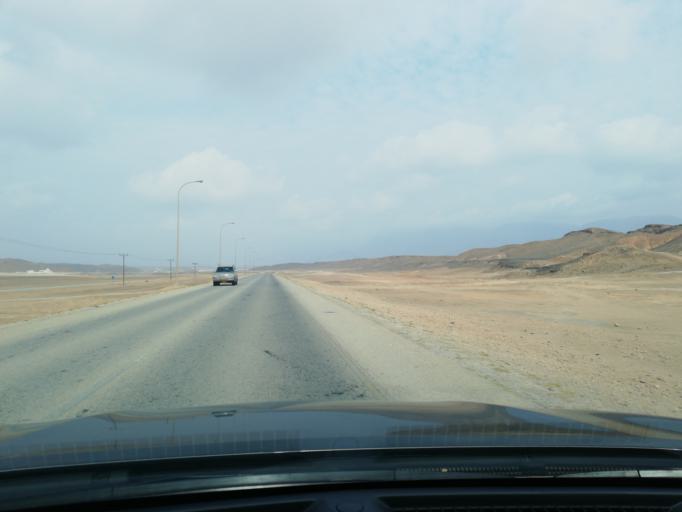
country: OM
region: Zufar
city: Salalah
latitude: 16.9584
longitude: 53.8992
